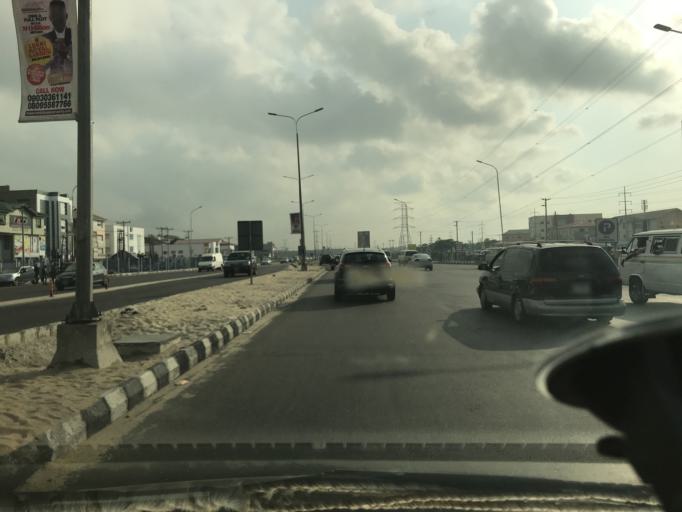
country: NG
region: Lagos
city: Ikoyi
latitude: 6.4385
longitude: 3.5217
